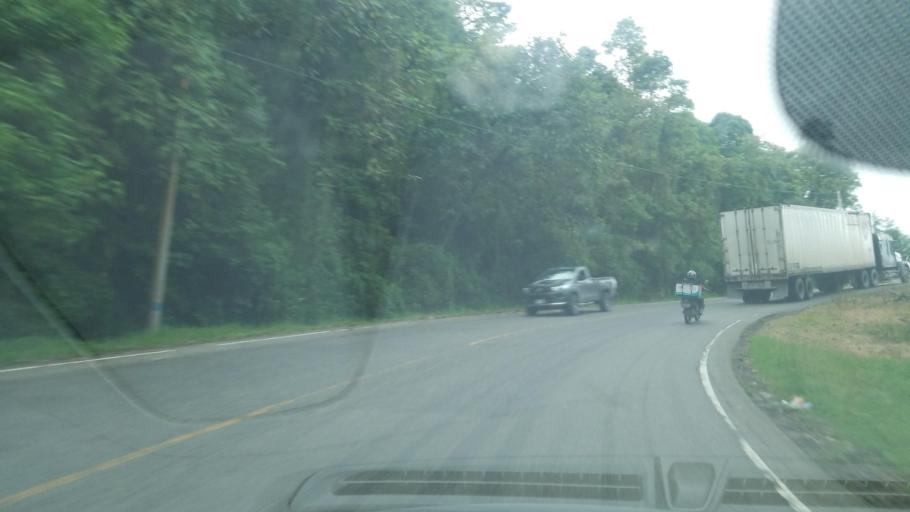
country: HN
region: Ocotepeque
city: La Labor
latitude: 14.4735
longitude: -89.0589
